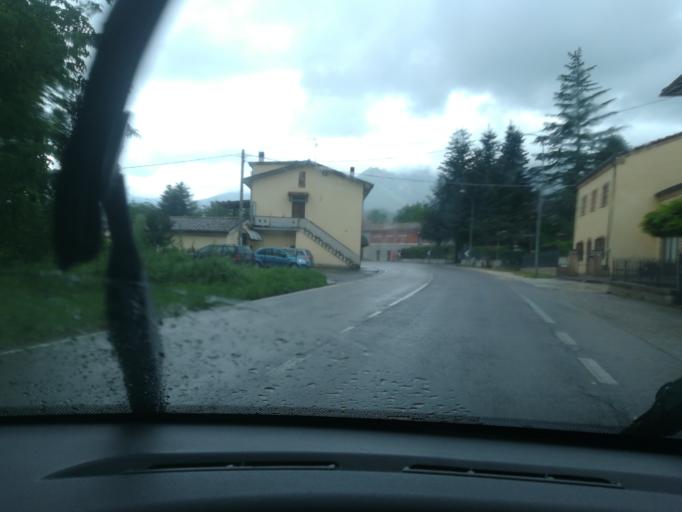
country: IT
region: The Marches
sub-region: Provincia di Macerata
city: Sarnano
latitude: 43.0542
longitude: 13.2729
